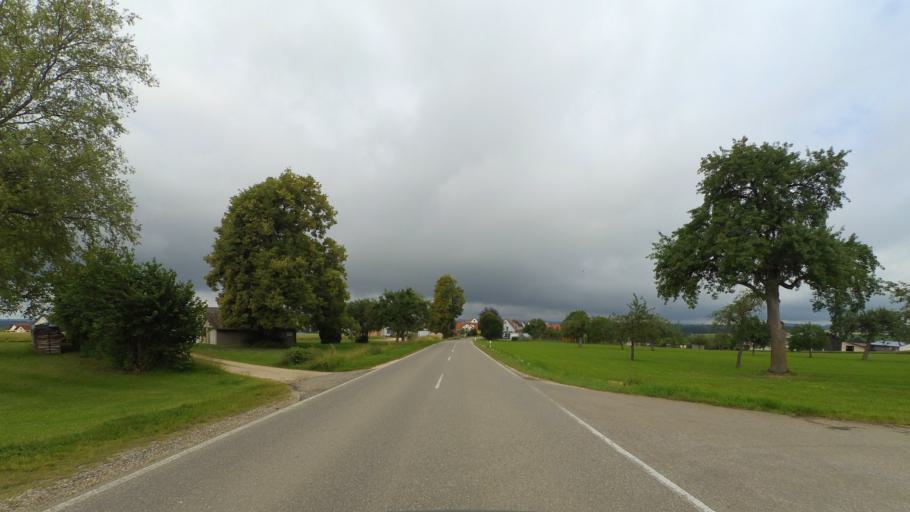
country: DE
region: Baden-Wuerttemberg
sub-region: Tuebingen Region
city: Lonsee
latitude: 48.5651
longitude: 9.9305
